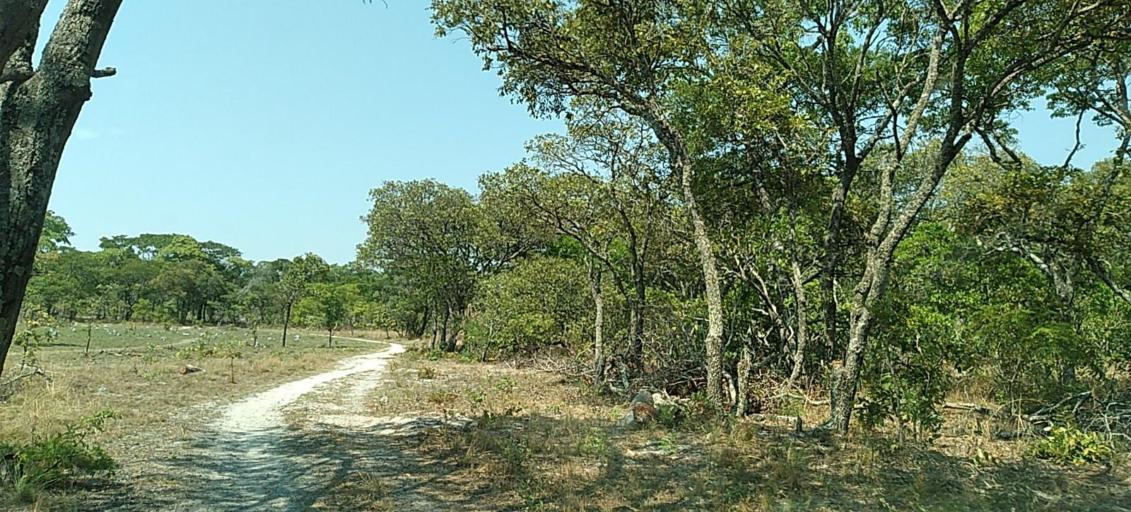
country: ZM
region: Copperbelt
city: Mpongwe
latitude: -13.7851
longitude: 28.1028
